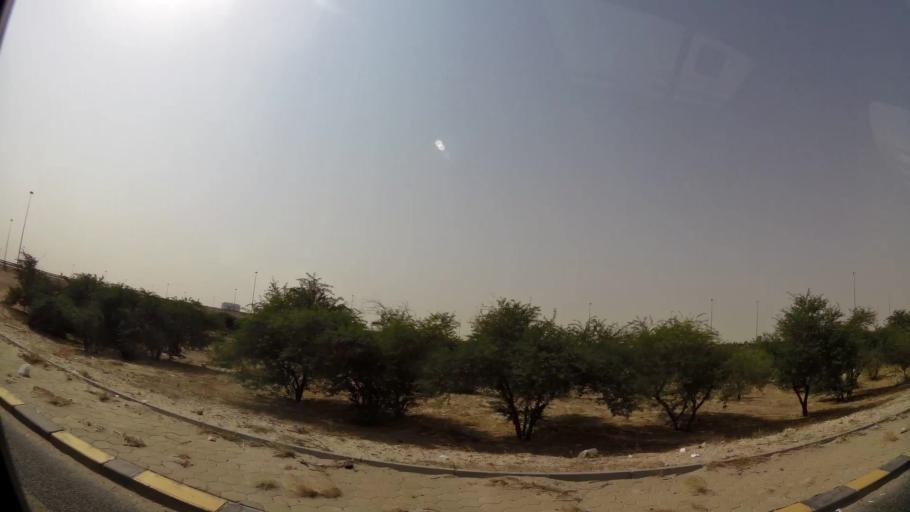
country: KW
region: Muhafazat al Jahra'
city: Al Jahra'
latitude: 29.3769
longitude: 47.6623
